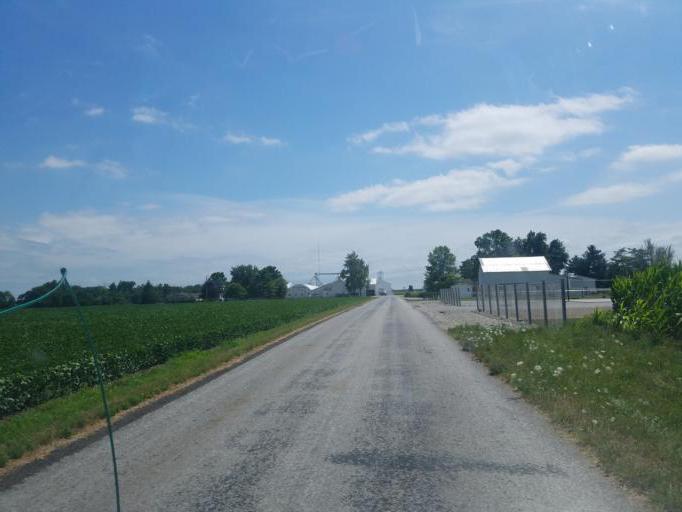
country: US
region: Indiana
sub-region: Allen County
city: Harlan
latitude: 41.1854
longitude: -84.8839
